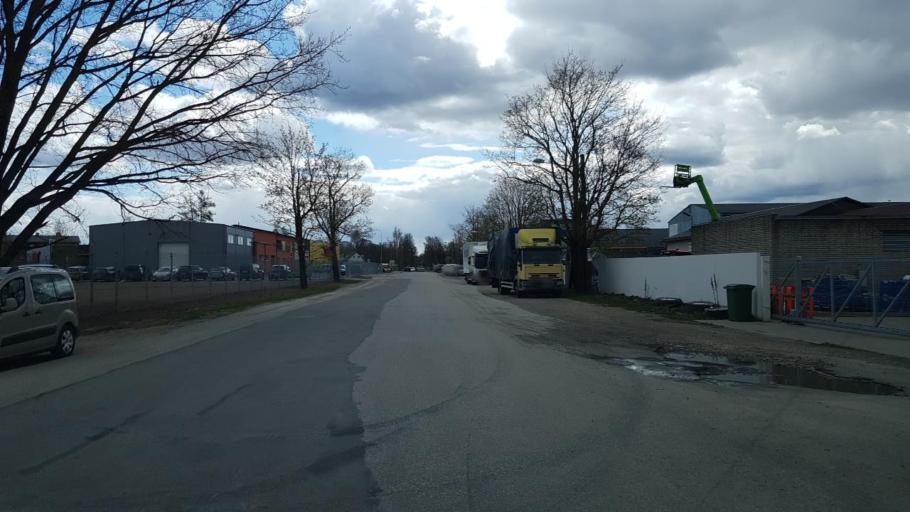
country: EE
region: Tartu
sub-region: Tartu linn
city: Tartu
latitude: 58.3781
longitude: 26.6956
